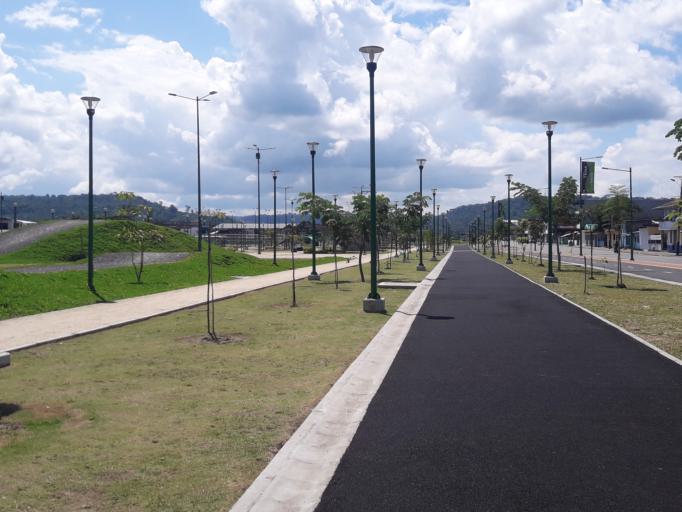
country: EC
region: Napo
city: Tena
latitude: -0.9864
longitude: -77.8218
